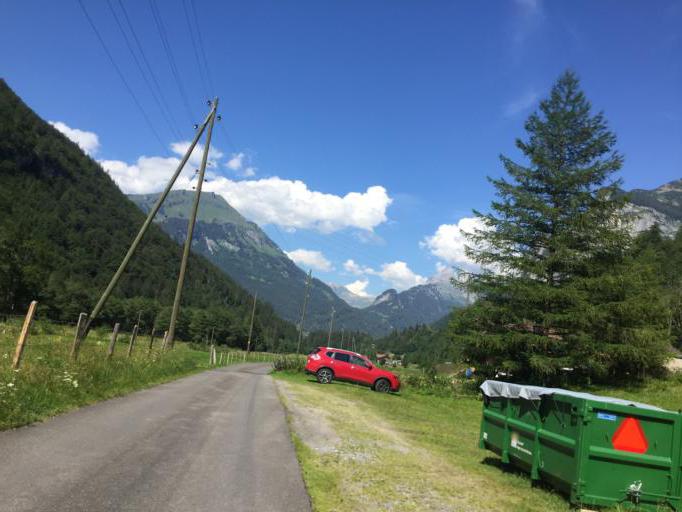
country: CH
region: Bern
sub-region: Interlaken-Oberhasli District
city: Meiringen
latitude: 46.6868
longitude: 8.2171
